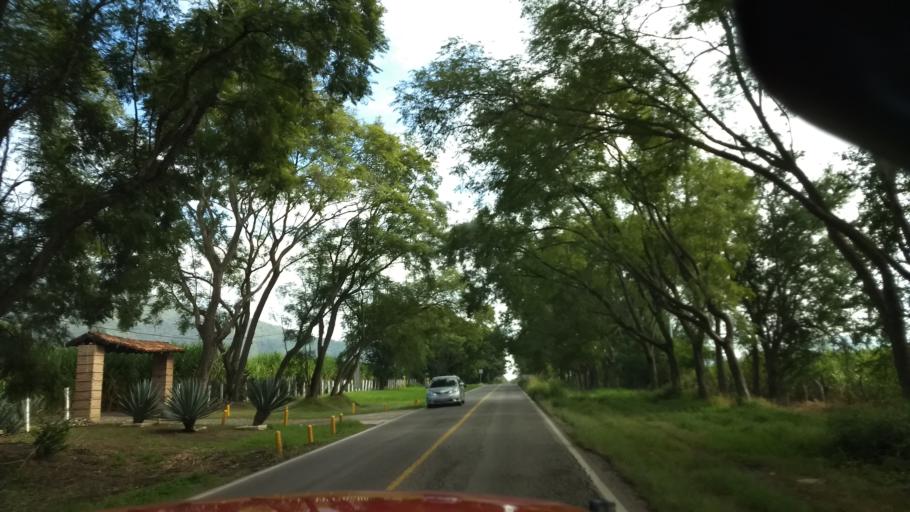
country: MX
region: Jalisco
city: Tuxpan
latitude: 19.5364
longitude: -103.4126
